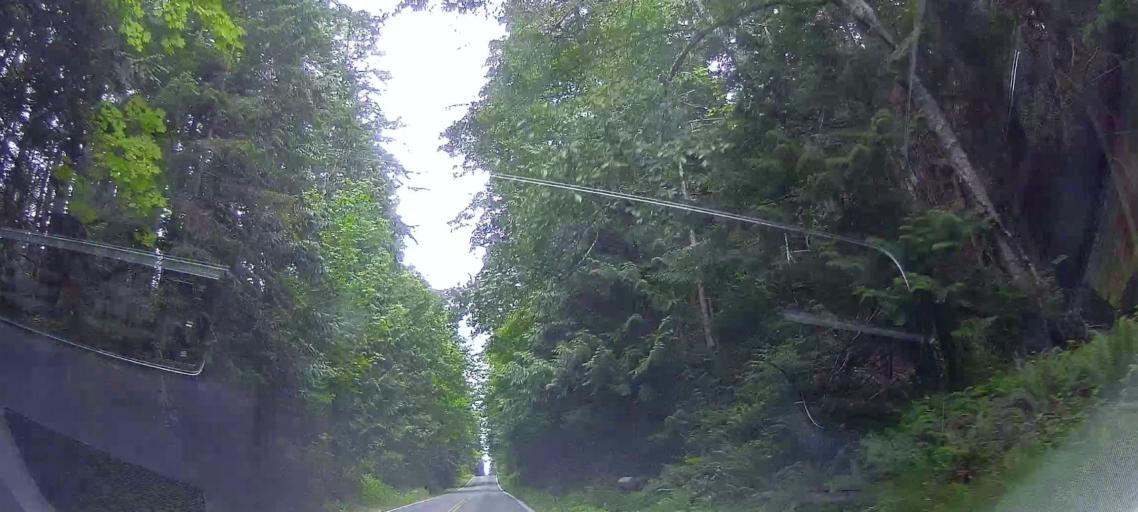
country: US
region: Washington
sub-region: Skagit County
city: Anacortes
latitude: 48.4623
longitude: -122.6343
